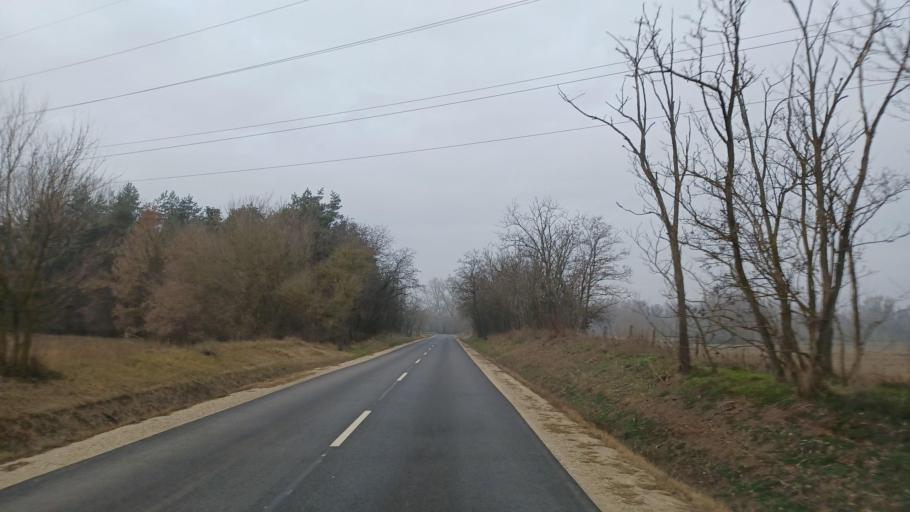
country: HU
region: Tolna
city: Paks
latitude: 46.6031
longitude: 18.8145
